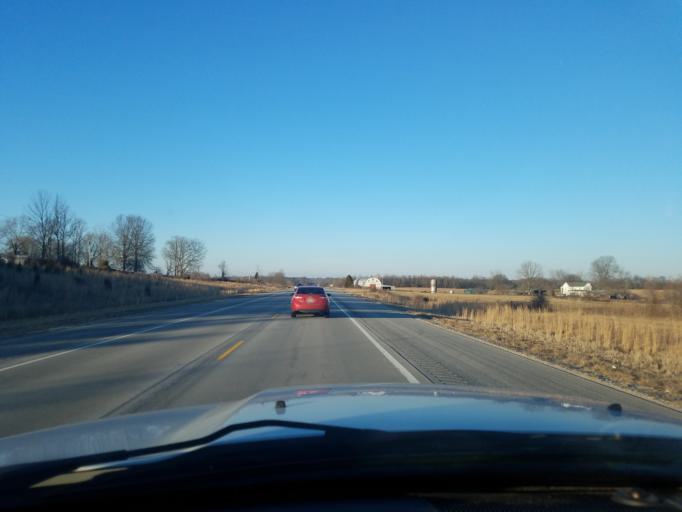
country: US
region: Indiana
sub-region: Crawford County
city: English
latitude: 38.2115
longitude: -86.5938
